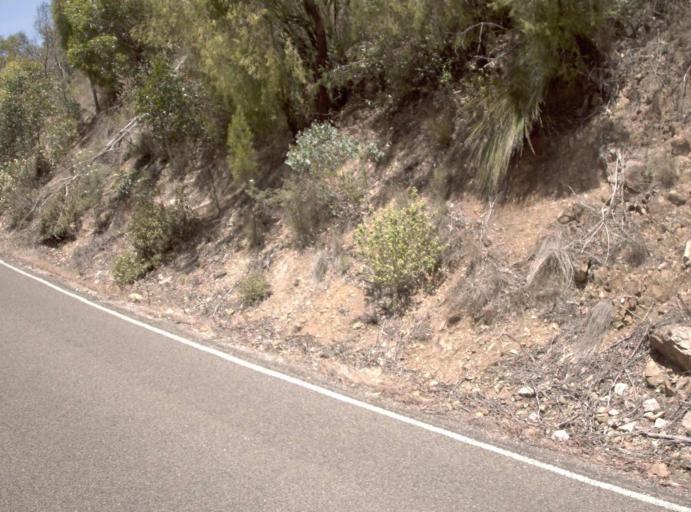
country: AU
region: Victoria
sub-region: East Gippsland
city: Lakes Entrance
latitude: -37.5706
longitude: 147.8907
